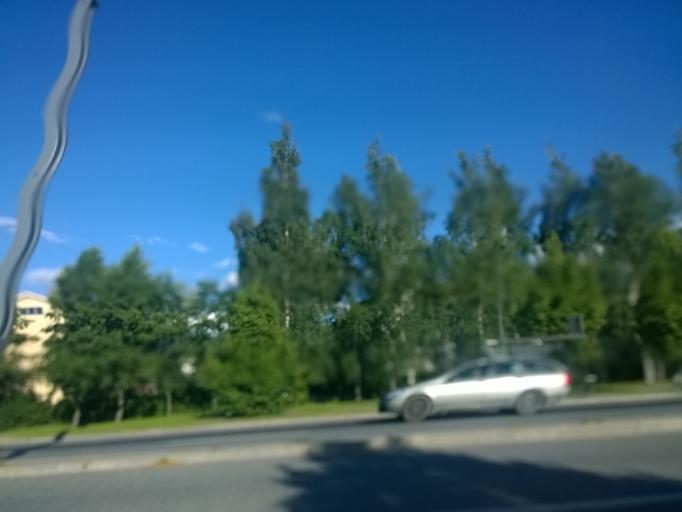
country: FI
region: Pirkanmaa
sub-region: Tampere
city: Tampere
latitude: 61.4826
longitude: 23.7763
